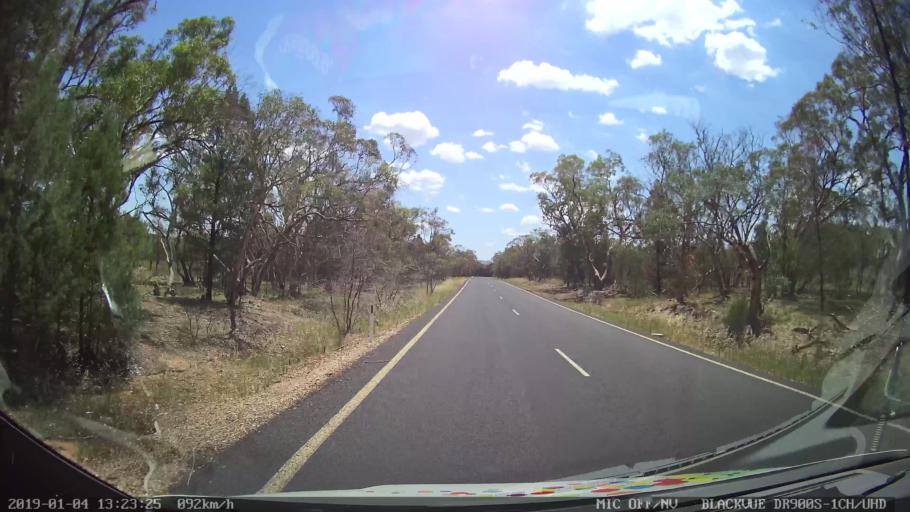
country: AU
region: New South Wales
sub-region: Parkes
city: Peak Hill
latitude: -32.7186
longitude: 148.5545
